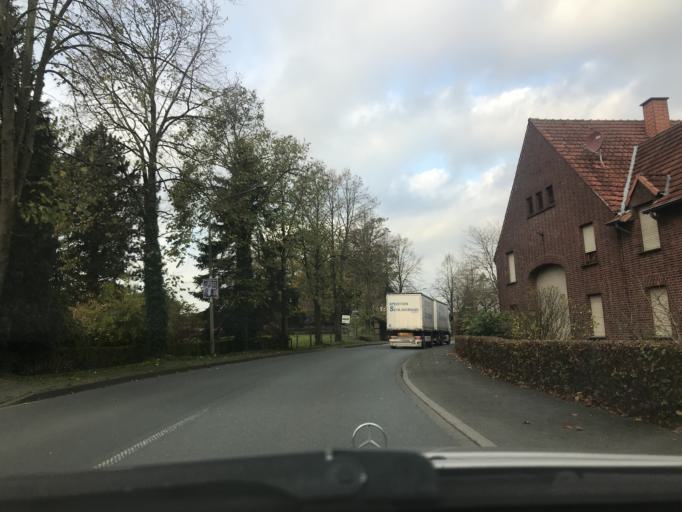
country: DE
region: North Rhine-Westphalia
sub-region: Regierungsbezirk Arnsberg
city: Soest
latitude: 51.6503
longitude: 8.0565
